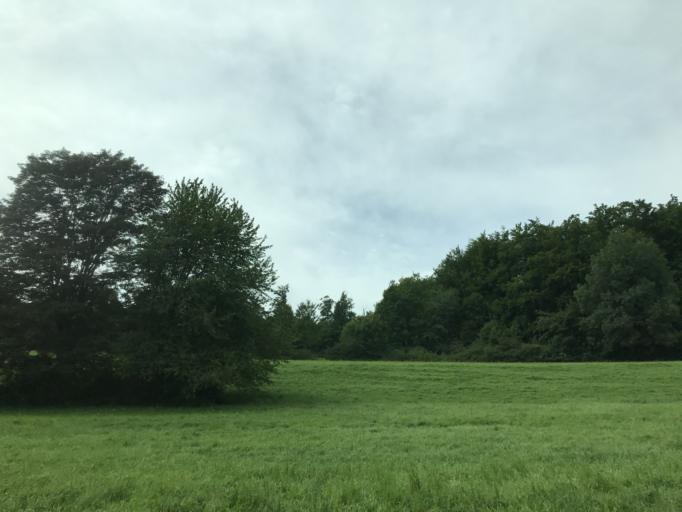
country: DE
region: Thuringia
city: Worbis
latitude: 51.4316
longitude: 10.3534
